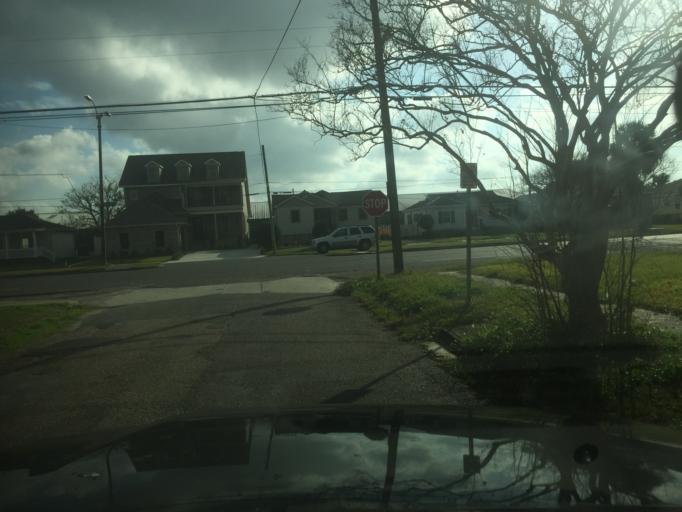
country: US
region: Louisiana
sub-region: Orleans Parish
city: New Orleans
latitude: 29.9894
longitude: -90.0841
